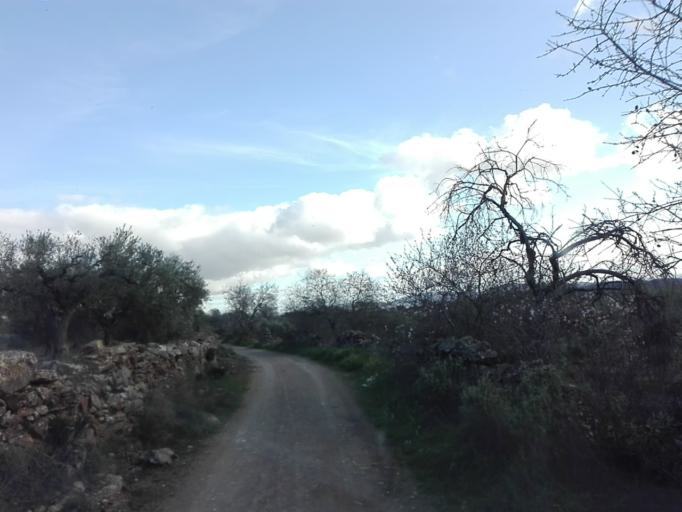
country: ES
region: Extremadura
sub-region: Provincia de Badajoz
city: Trasierra
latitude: 38.1875
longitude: -5.9902
